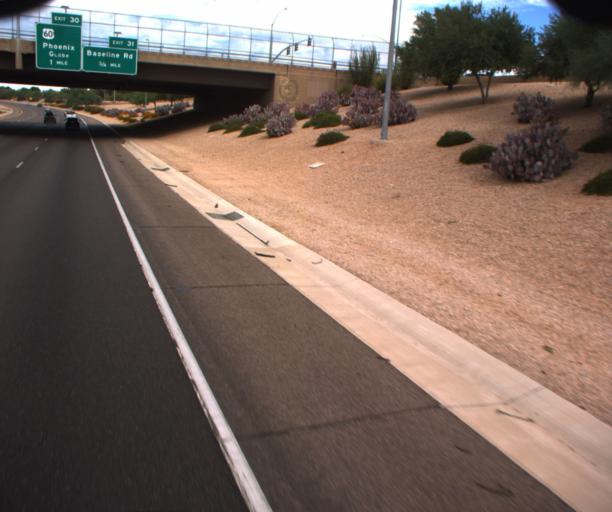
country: US
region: Arizona
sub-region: Pinal County
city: Apache Junction
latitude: 33.3640
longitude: -111.6438
